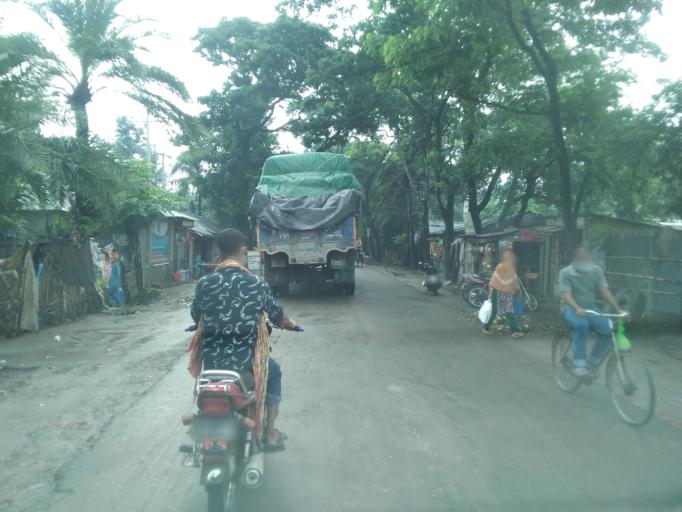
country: IN
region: West Bengal
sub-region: North 24 Parganas
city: Taki
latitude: 22.3479
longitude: 89.1037
